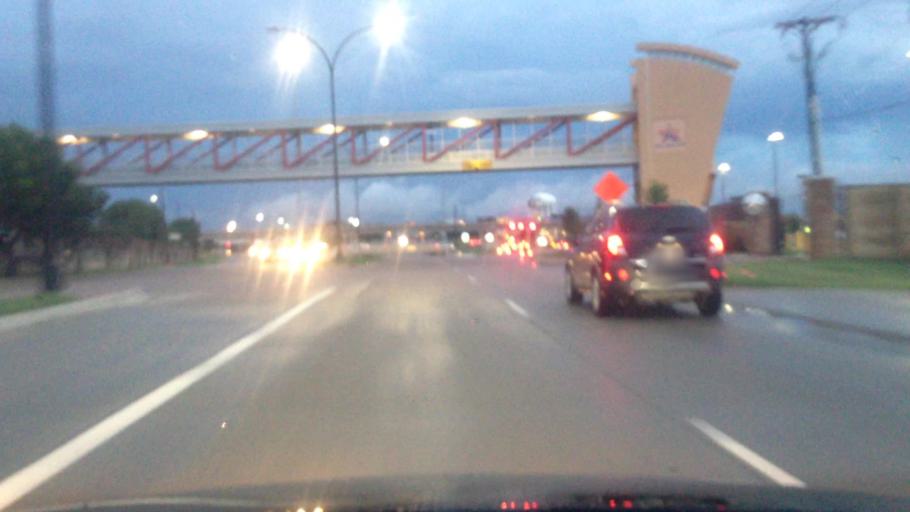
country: US
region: Texas
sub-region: Tarrant County
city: Arlington
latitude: 32.7355
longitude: -97.0655
